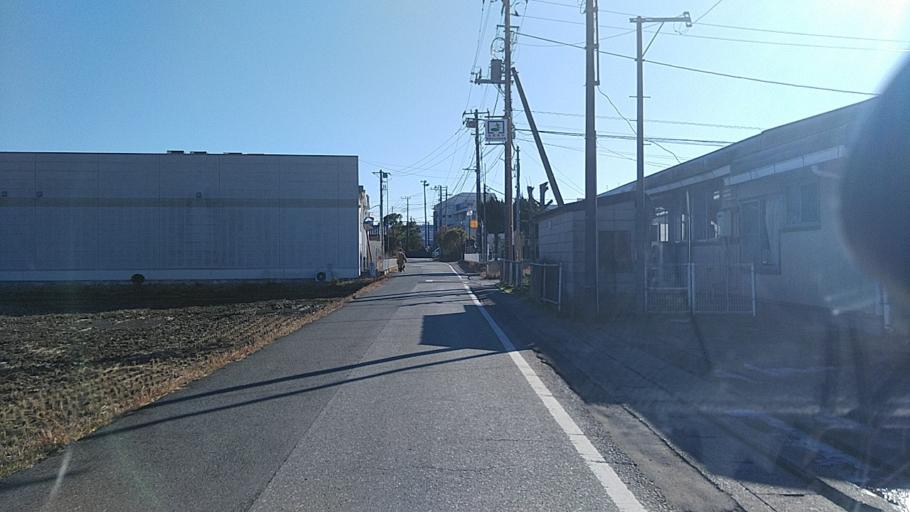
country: JP
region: Chiba
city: Kimitsu
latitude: 35.3050
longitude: 139.9567
